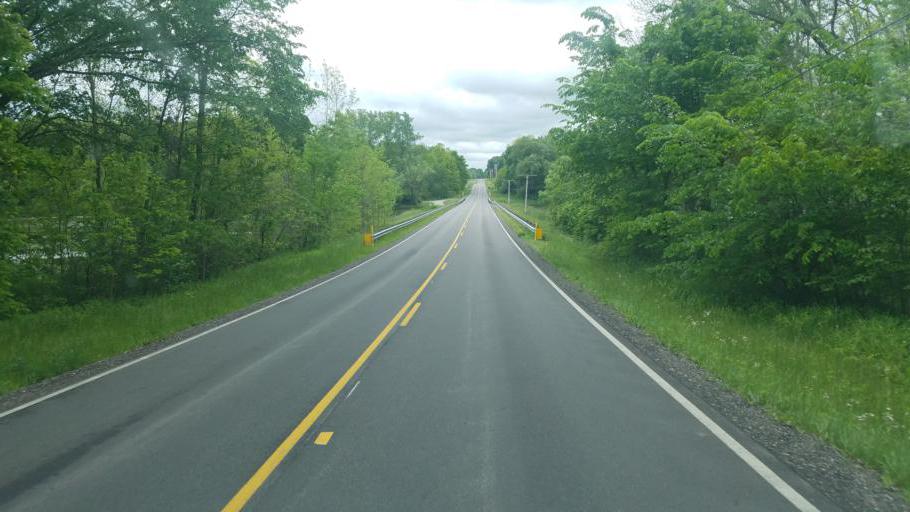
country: US
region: Ohio
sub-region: Portage County
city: Mantua
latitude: 41.3717
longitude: -81.2460
